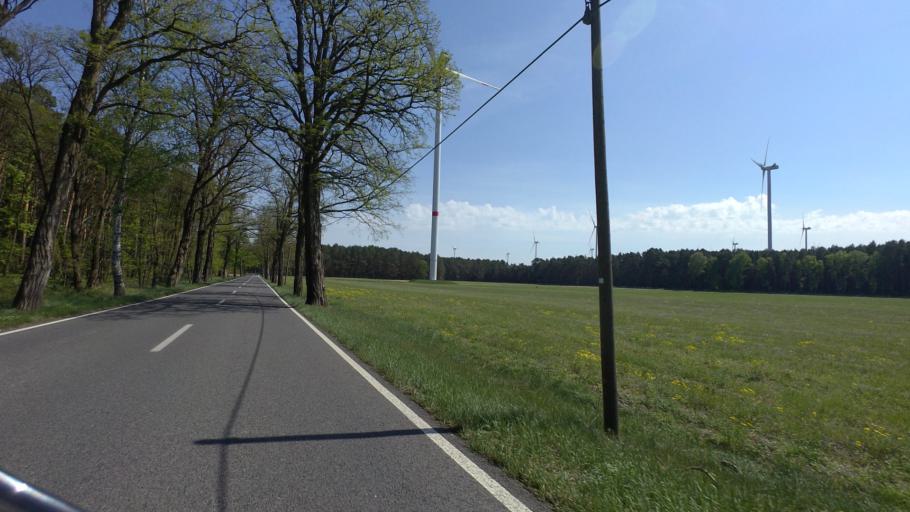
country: DE
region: Brandenburg
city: Neu Zauche
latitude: 51.9949
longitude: 14.0988
